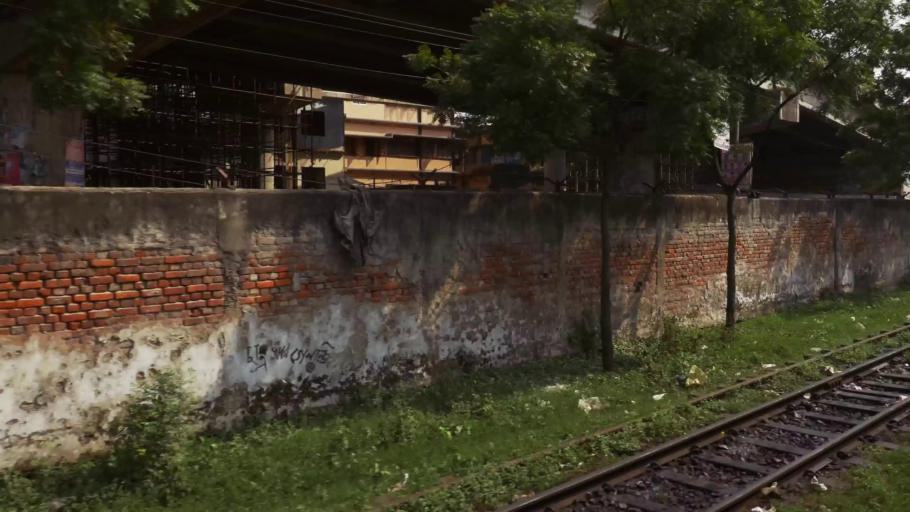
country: BD
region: Dhaka
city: Paltan
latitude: 23.7485
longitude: 90.4214
